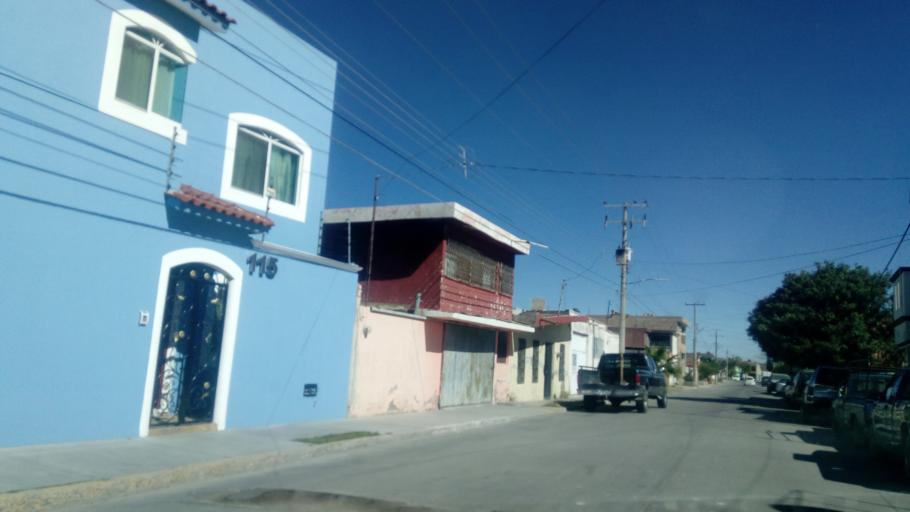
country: MX
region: Durango
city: Victoria de Durango
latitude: 24.0165
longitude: -104.6436
